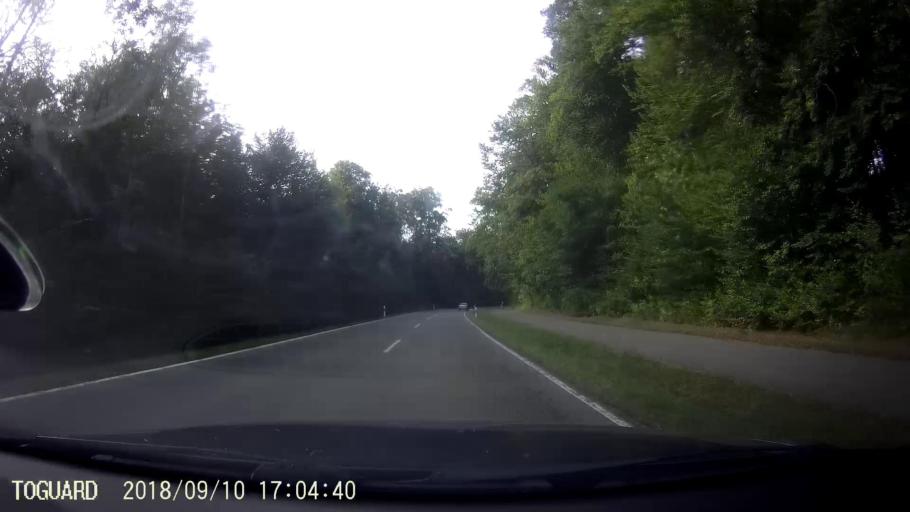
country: CH
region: Thurgau
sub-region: Kreuzlingen District
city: Gottlieben
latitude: 47.7155
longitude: 9.1309
